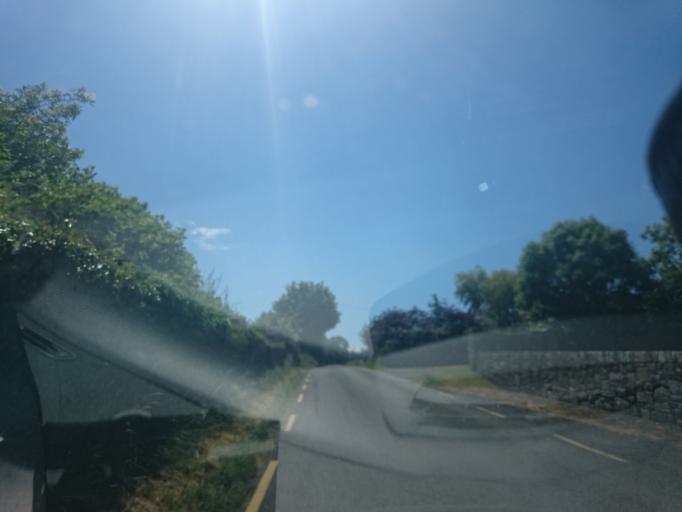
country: IE
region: Leinster
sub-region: County Carlow
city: Bagenalstown
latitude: 52.6215
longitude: -6.9913
